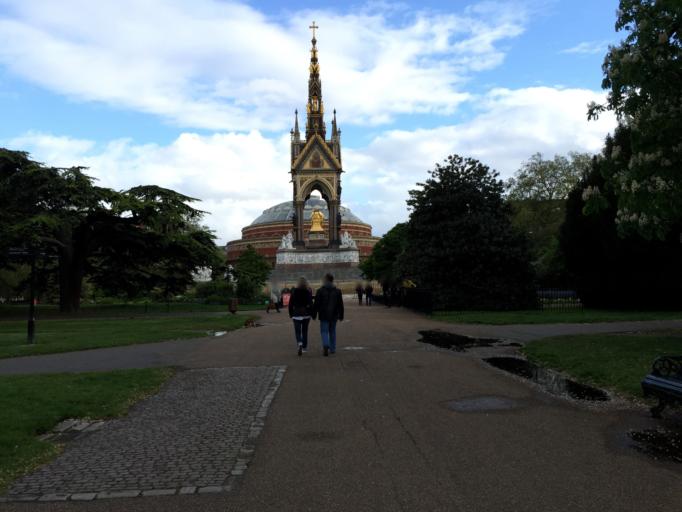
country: GB
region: England
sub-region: Greater London
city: Bayswater
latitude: 51.5034
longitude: -0.1778
